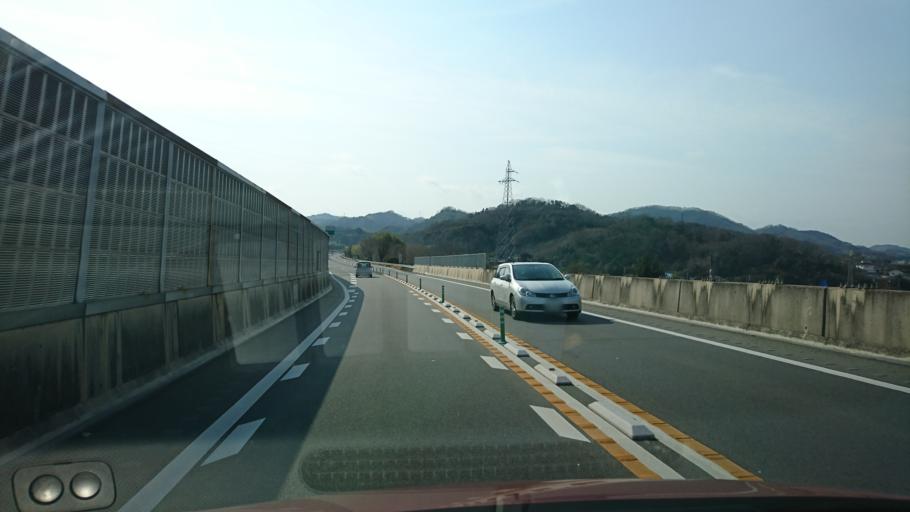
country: JP
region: Hiroshima
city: Onomichi
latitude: 34.3996
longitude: 133.2091
